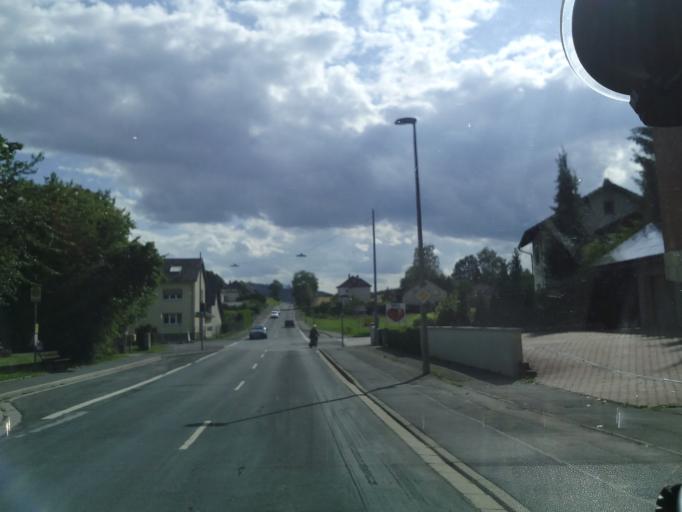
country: DE
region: Bavaria
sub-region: Upper Franconia
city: Neustadt bei Coburg
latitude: 50.3181
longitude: 11.1015
